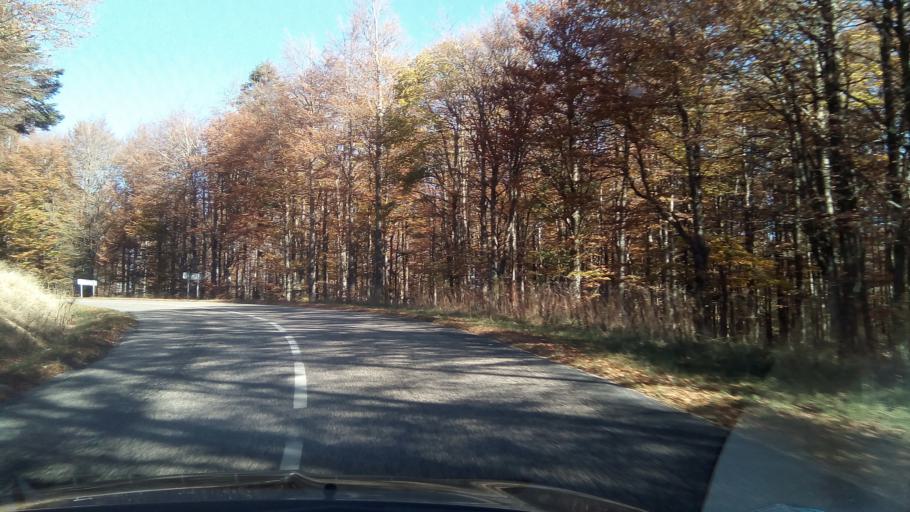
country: FR
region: Alsace
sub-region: Departement du Bas-Rhin
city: Ville
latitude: 48.3882
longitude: 7.2657
